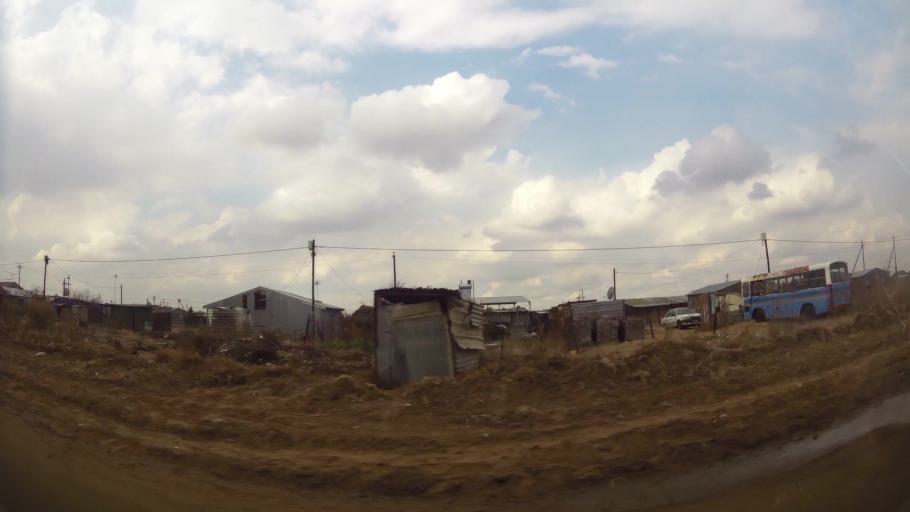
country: ZA
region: Orange Free State
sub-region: Fezile Dabi District Municipality
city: Sasolburg
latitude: -26.8650
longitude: 27.8946
